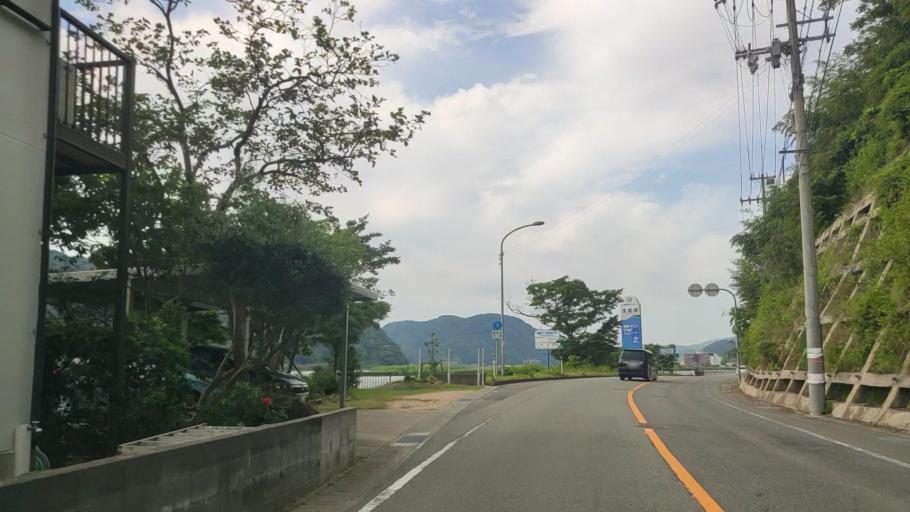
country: JP
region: Hyogo
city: Toyooka
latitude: 35.6399
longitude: 134.8232
